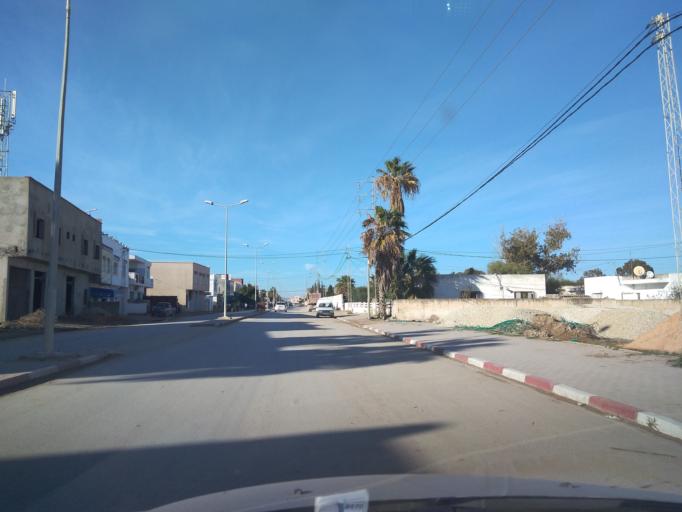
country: TN
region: Ariana
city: Qal'at al Andalus
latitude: 37.0560
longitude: 10.1208
